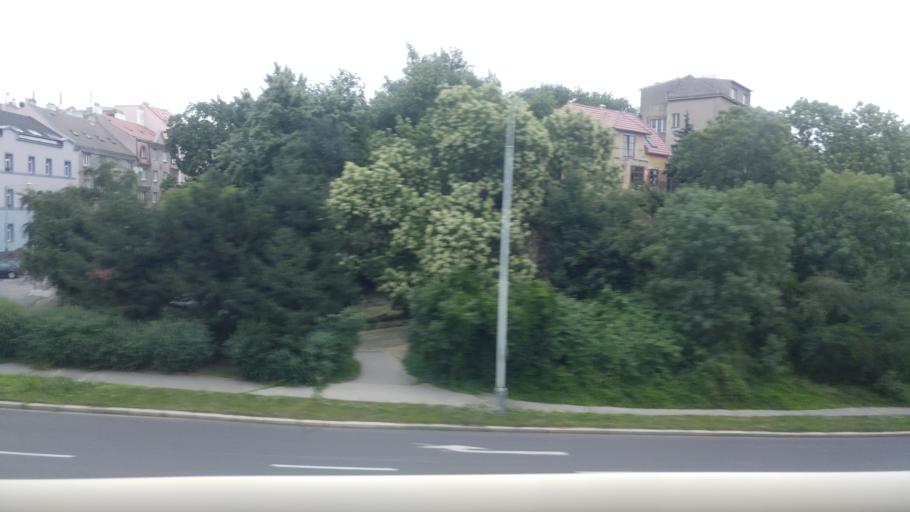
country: CZ
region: Praha
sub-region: Praha 8
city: Liben
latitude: 50.1110
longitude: 14.4769
